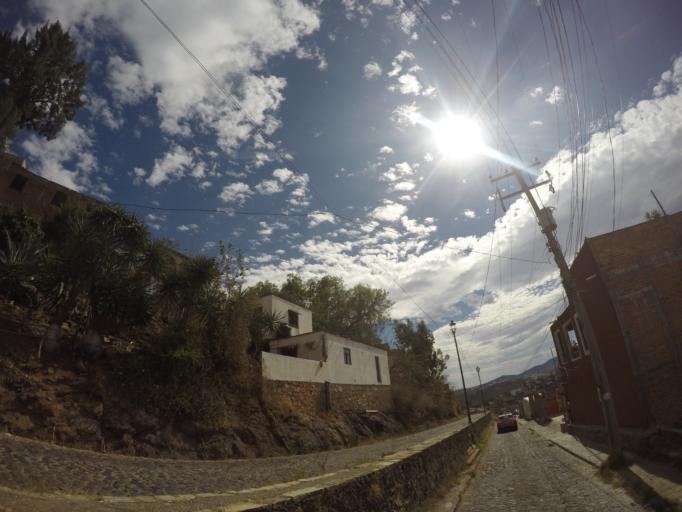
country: MX
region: Guanajuato
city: Guanajuato
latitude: 21.0155
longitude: -101.2621
